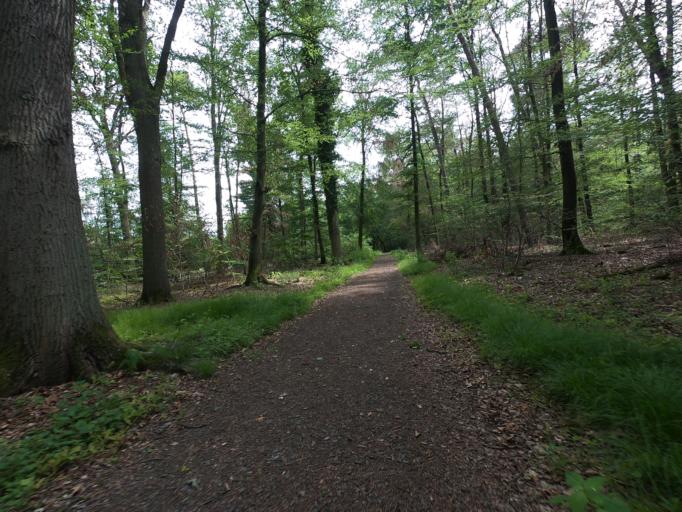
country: DE
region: Hesse
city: Heusenstamm
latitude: 50.0605
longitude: 8.7721
